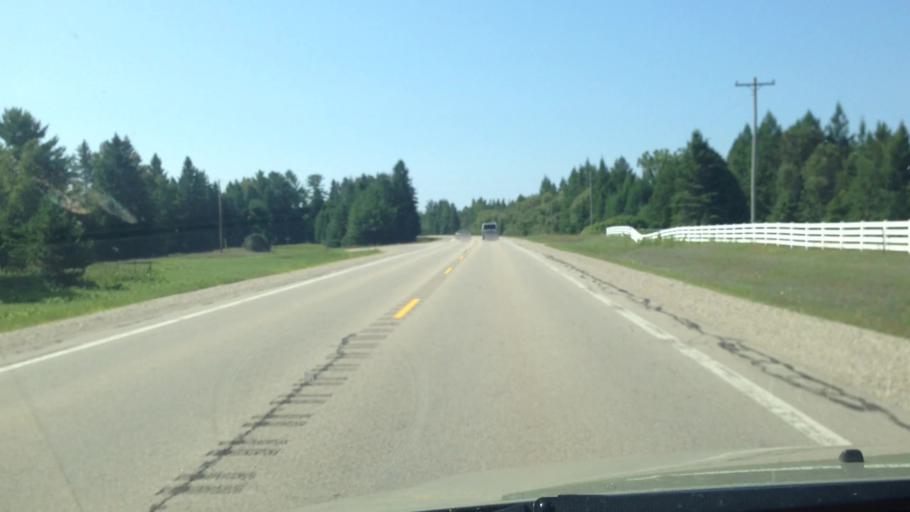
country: US
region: Michigan
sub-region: Delta County
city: Escanaba
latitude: 45.5239
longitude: -87.2880
